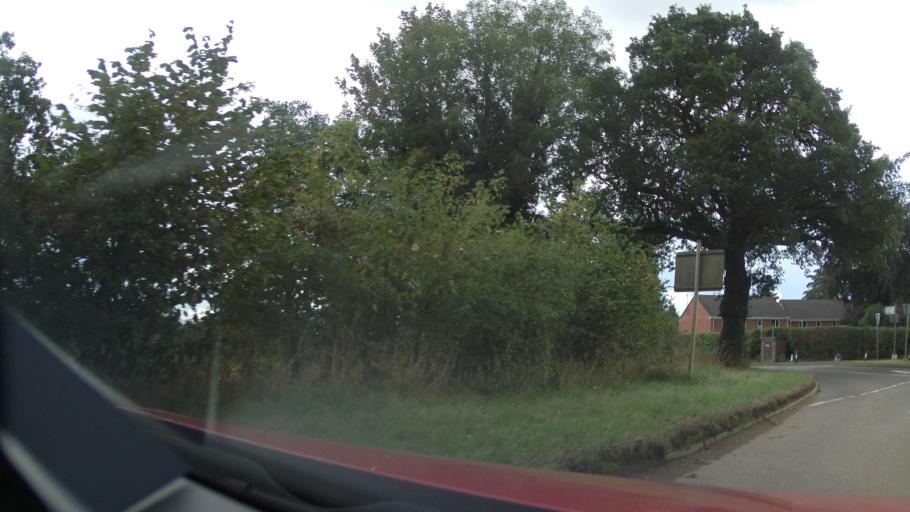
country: GB
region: England
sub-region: Staffordshire
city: Eccleshall
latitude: 52.8934
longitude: -2.2158
